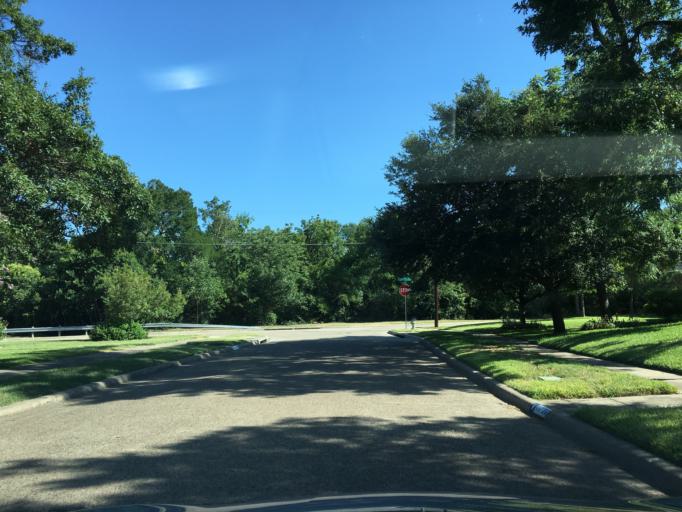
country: US
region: Texas
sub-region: Dallas County
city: Garland
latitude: 32.8539
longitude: -96.6956
